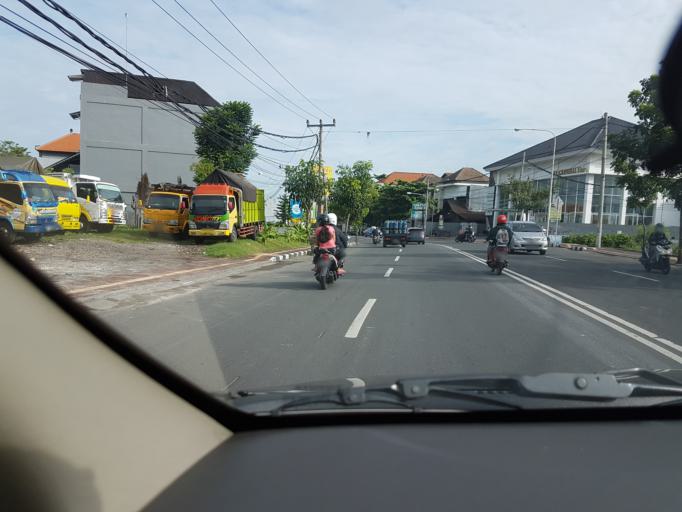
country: ID
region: Bali
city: Denpasar
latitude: -8.6716
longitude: 115.1914
